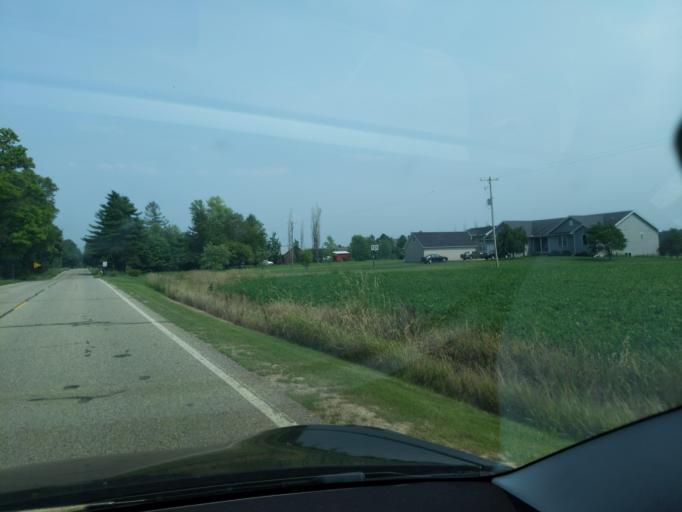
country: US
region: Michigan
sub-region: Clinton County
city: Saint Johns
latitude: 42.9291
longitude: -84.5716
